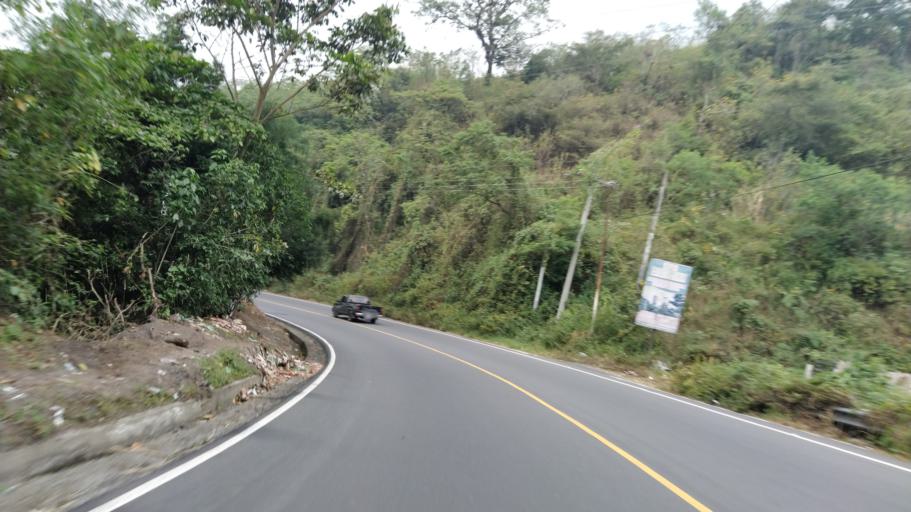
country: GT
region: Quetzaltenango
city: Zunil
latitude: 14.7297
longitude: -91.5243
